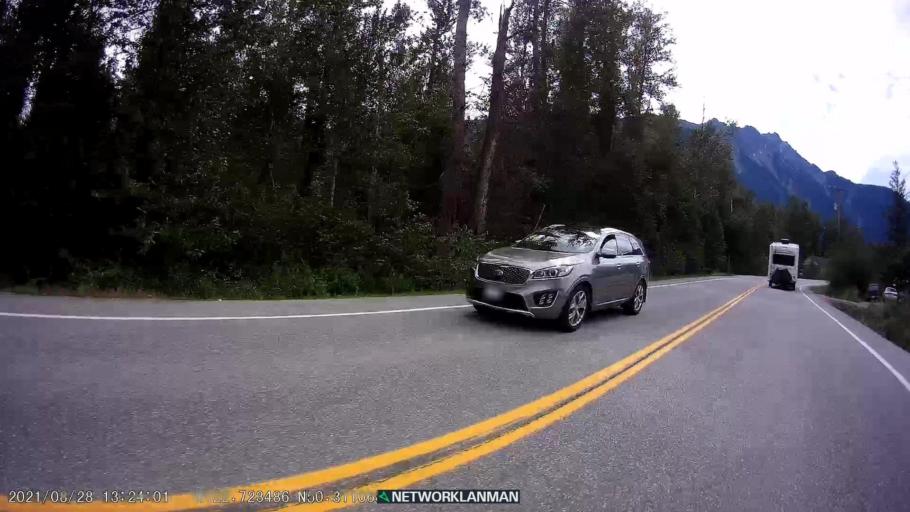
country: CA
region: British Columbia
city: Pemberton
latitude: 50.3111
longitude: -122.7217
